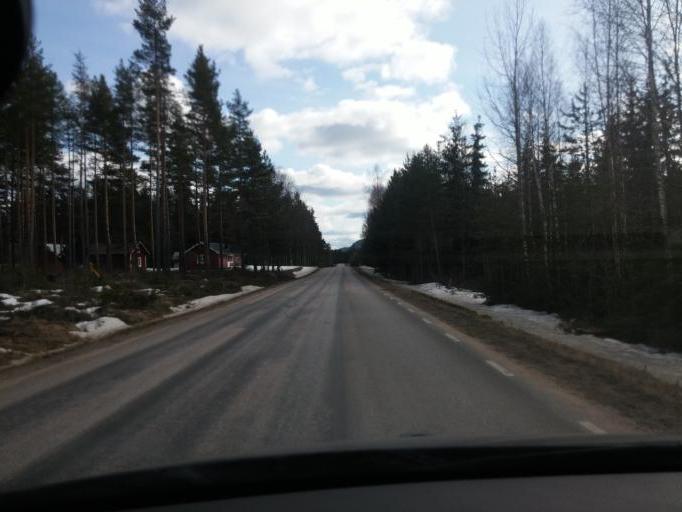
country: SE
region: Gaevleborg
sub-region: Ljusdals Kommun
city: Ljusdal
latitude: 61.8109
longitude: 16.1526
